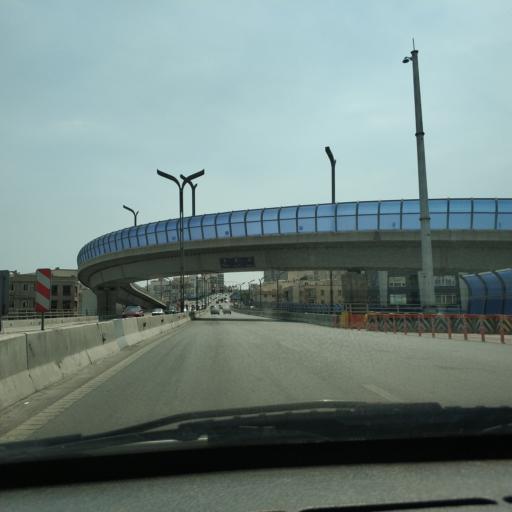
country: IR
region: Tehran
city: Tajrish
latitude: 35.7914
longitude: 51.4564
